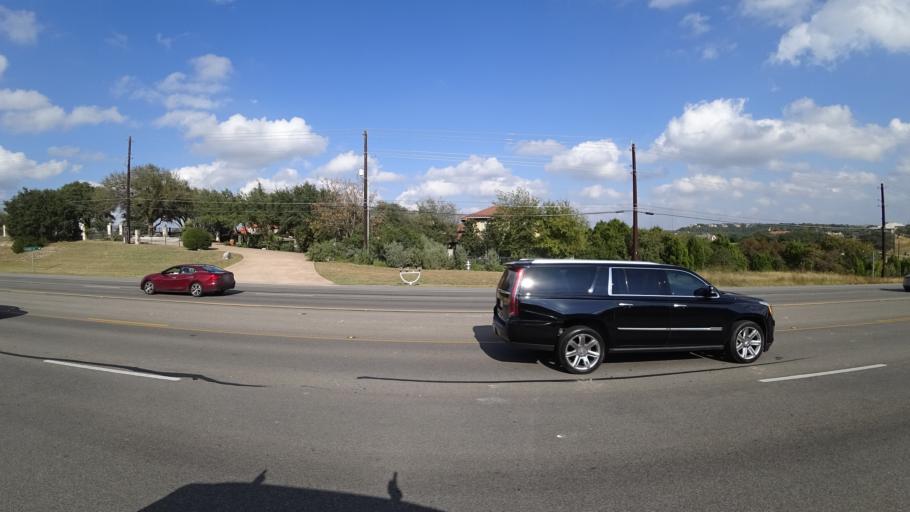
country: US
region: Texas
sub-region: Travis County
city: Lost Creek
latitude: 30.3109
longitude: -97.8492
